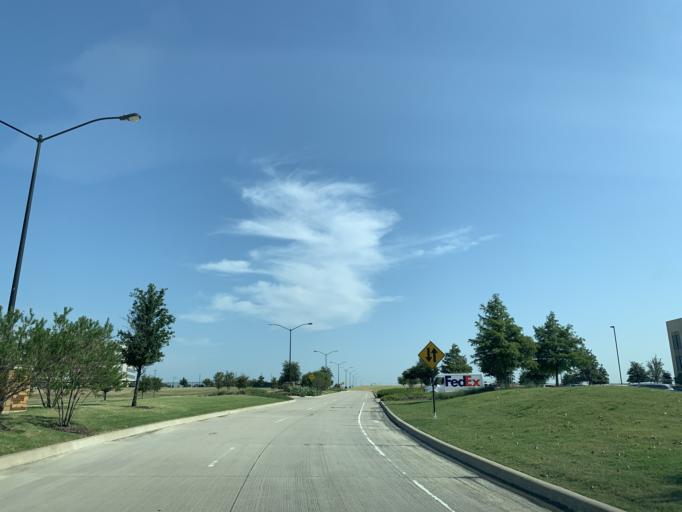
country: US
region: Texas
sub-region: Tarrant County
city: Keller
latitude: 32.9181
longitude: -97.3123
